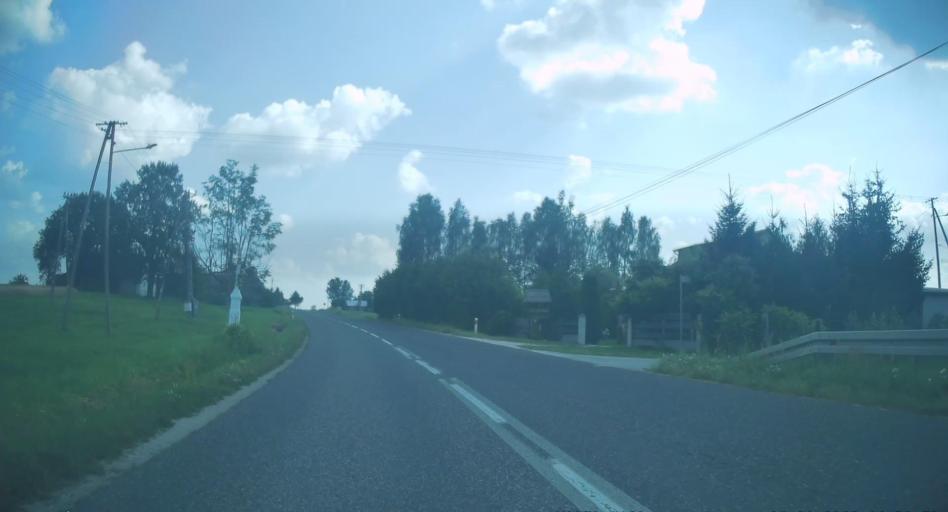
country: PL
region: Swietokrzyskie
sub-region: Powiat kielecki
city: Lopuszno
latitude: 50.9094
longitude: 20.2452
